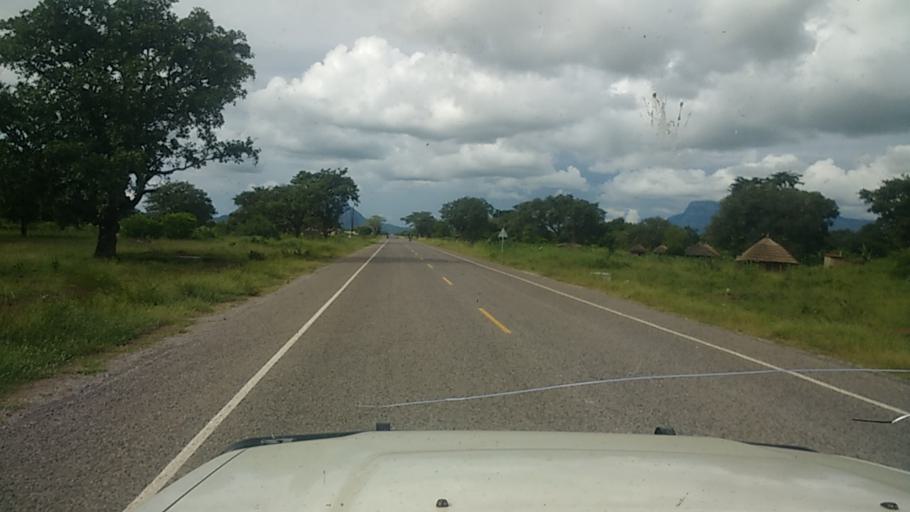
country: UG
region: Eastern Region
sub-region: Katakwi District
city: Katakwi
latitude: 2.0247
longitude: 34.1191
